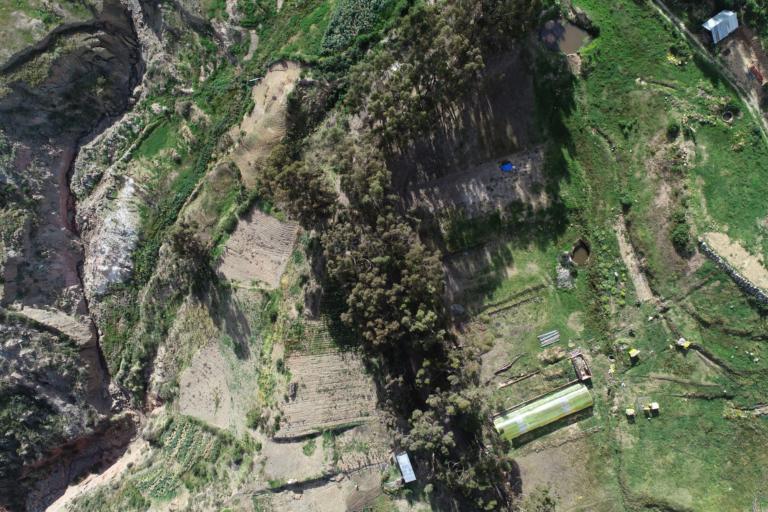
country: BO
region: La Paz
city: La Paz
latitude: -16.5505
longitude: -67.9933
